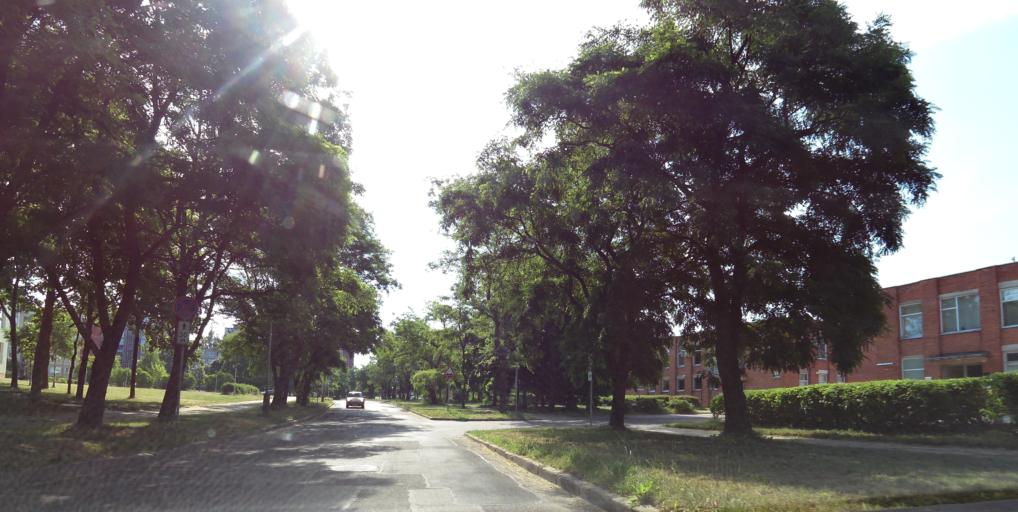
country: LT
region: Vilnius County
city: Pilaite
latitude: 54.6913
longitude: 25.2052
